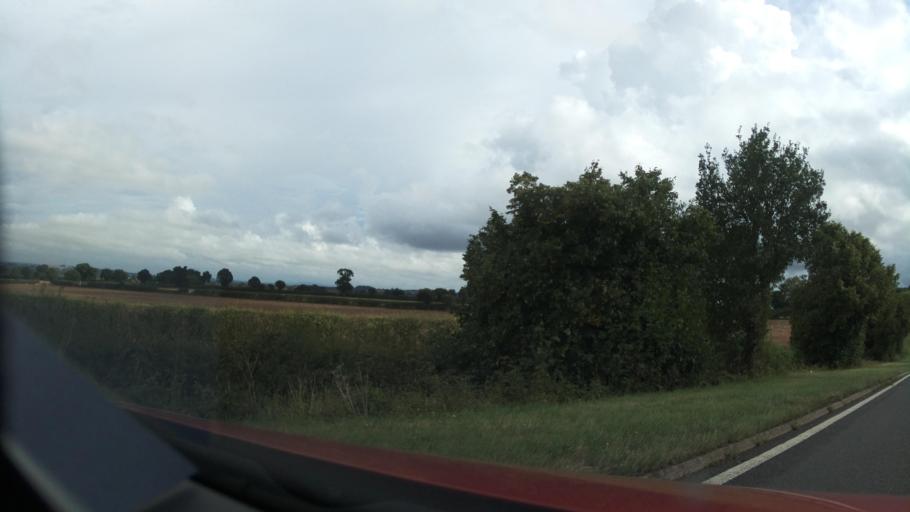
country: GB
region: England
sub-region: Shropshire
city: Bridgnorth
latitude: 52.5796
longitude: -2.3948
